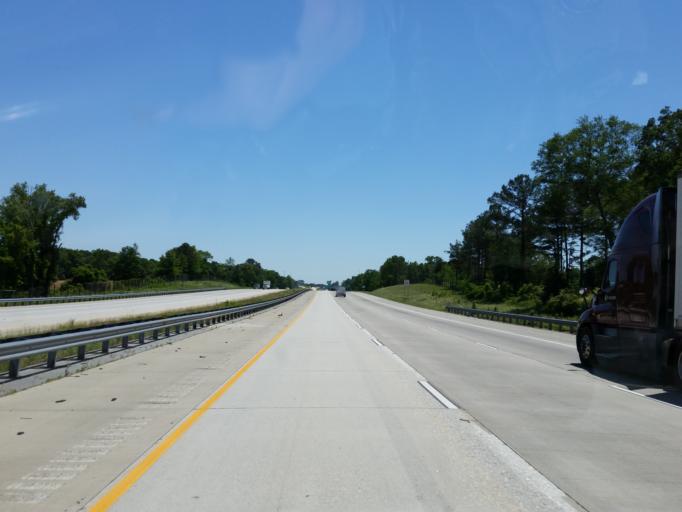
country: US
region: Georgia
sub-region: Dooly County
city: Unadilla
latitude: 32.2770
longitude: -83.7548
